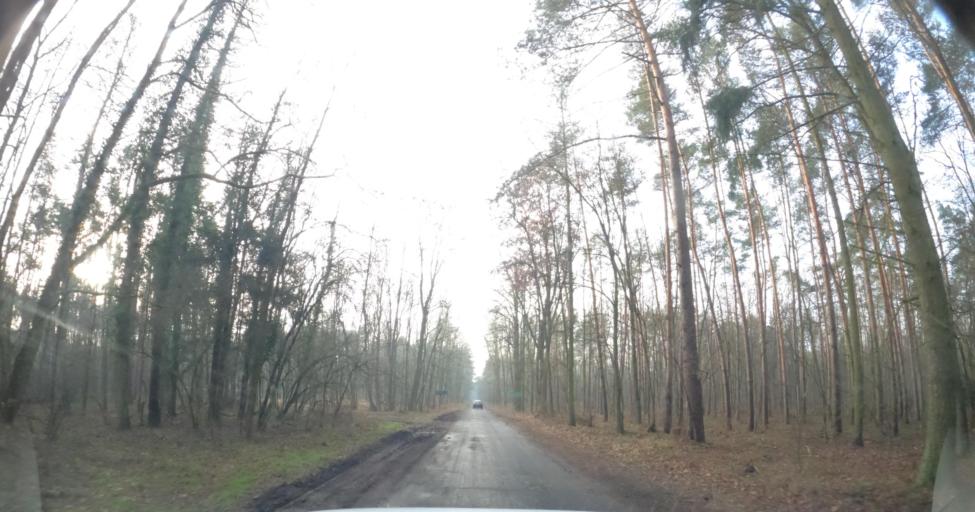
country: PL
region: West Pomeranian Voivodeship
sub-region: Powiat mysliborski
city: Boleszkowice
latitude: 52.7164
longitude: 14.5601
